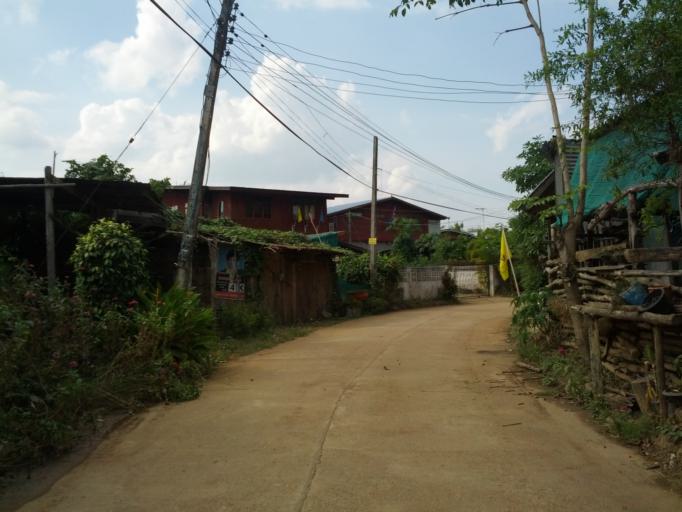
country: TH
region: Sukhothai
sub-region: Amphoe Si Satchanalai
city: Si Satchanalai
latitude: 17.4280
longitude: 99.6876
